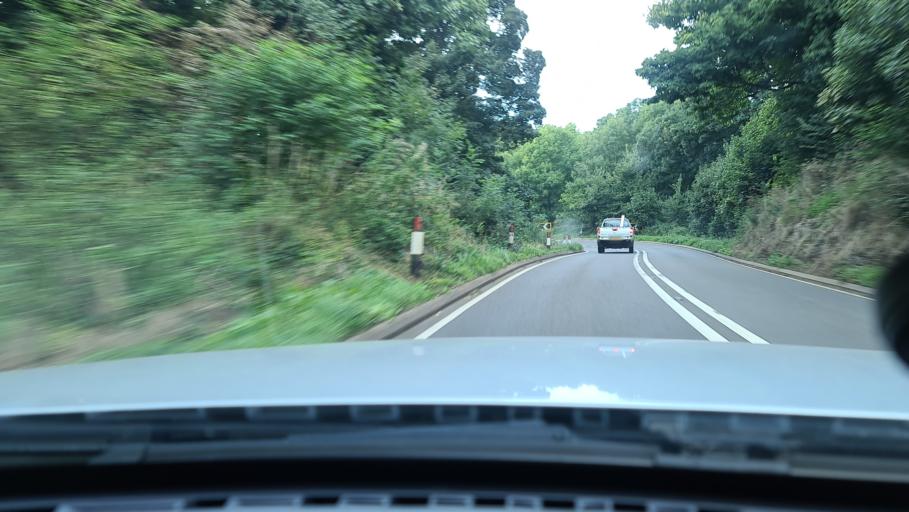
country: GB
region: England
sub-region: Oxfordshire
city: Hanwell
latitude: 52.1114
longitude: -1.4761
